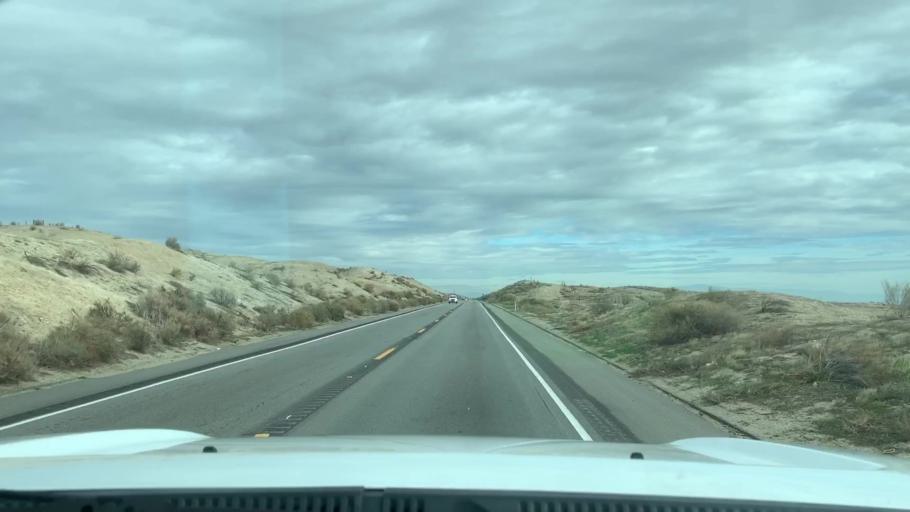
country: US
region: California
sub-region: Kern County
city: Ford City
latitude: 35.2351
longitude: -119.3663
